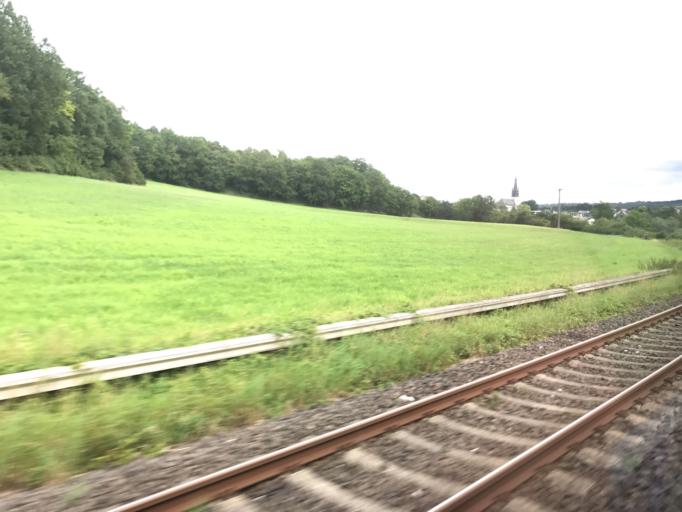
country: DE
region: Hesse
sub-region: Regierungsbezirk Giessen
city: Villmar
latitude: 50.3926
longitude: 8.1792
